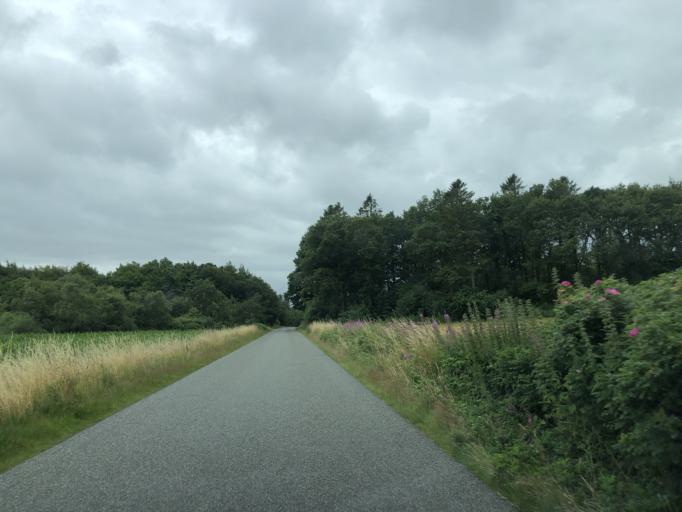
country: DK
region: Central Jutland
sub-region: Herning Kommune
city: Snejbjerg
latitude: 56.1952
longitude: 8.8450
